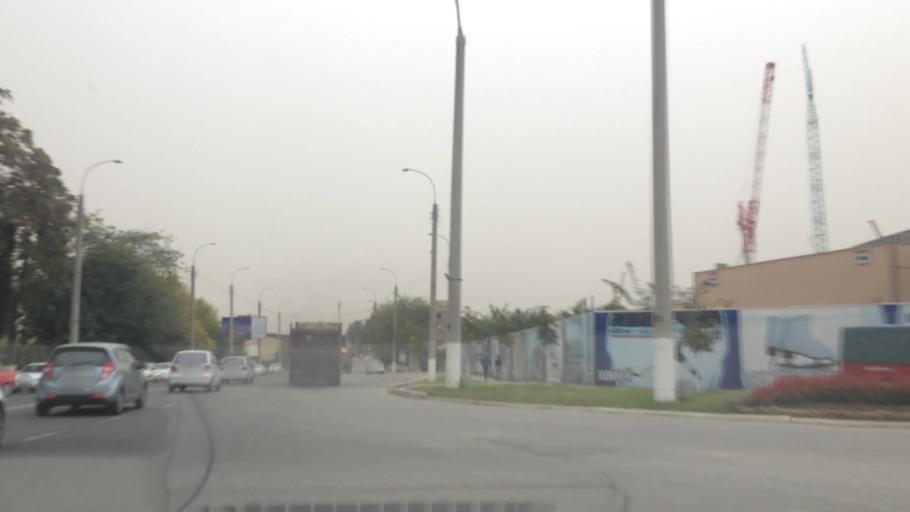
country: UZ
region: Toshkent Shahri
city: Tashkent
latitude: 41.3078
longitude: 69.2551
